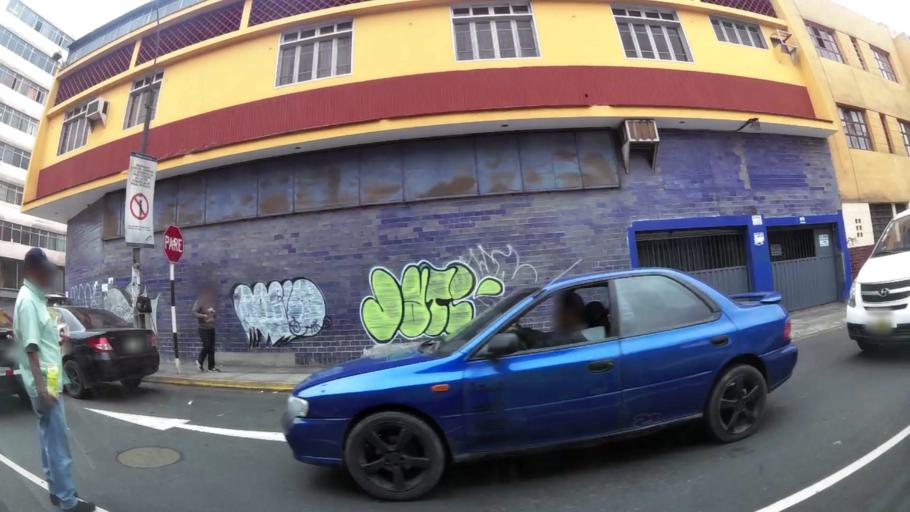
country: PE
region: Lima
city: Lima
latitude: -12.0507
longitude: -77.0409
